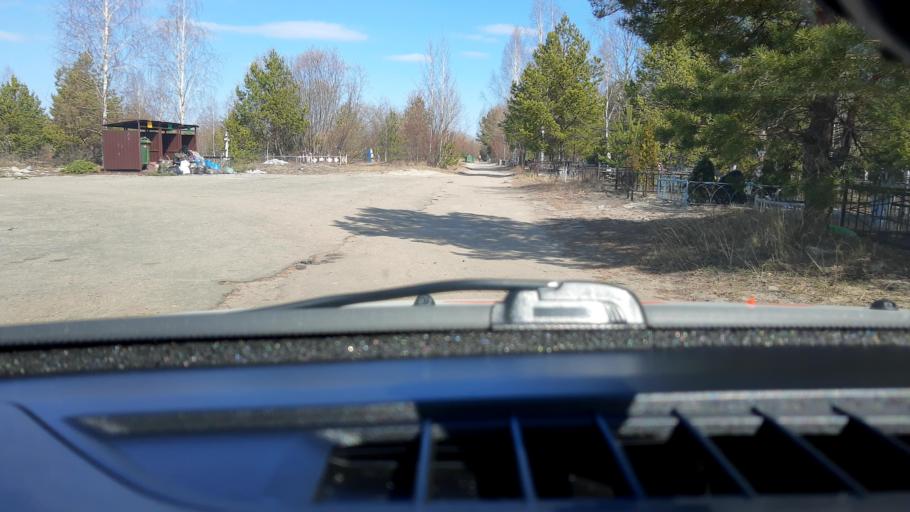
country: RU
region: Nizjnij Novgorod
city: Gorbatovka
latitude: 56.3550
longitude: 43.7701
